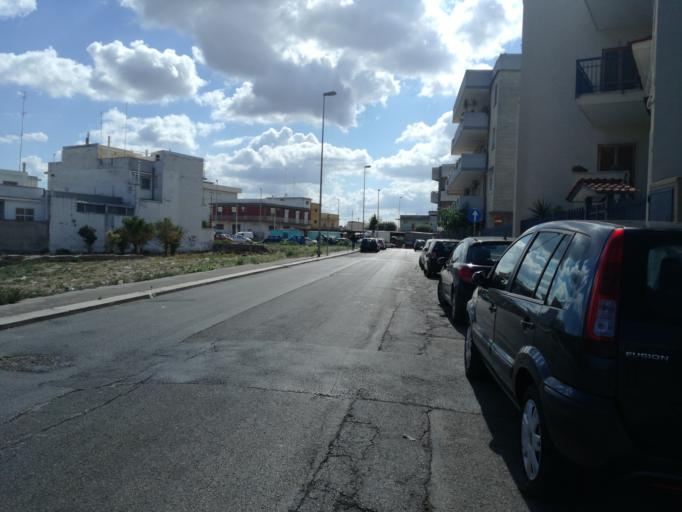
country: IT
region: Apulia
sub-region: Provincia di Bari
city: Triggiano
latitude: 41.0649
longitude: 16.9295
